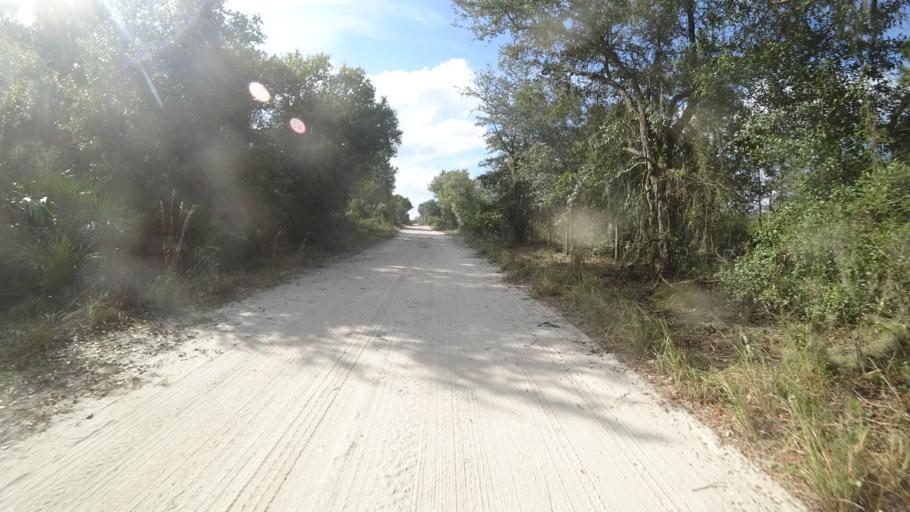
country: US
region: Florida
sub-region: DeSoto County
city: Arcadia
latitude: 27.3540
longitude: -82.1207
